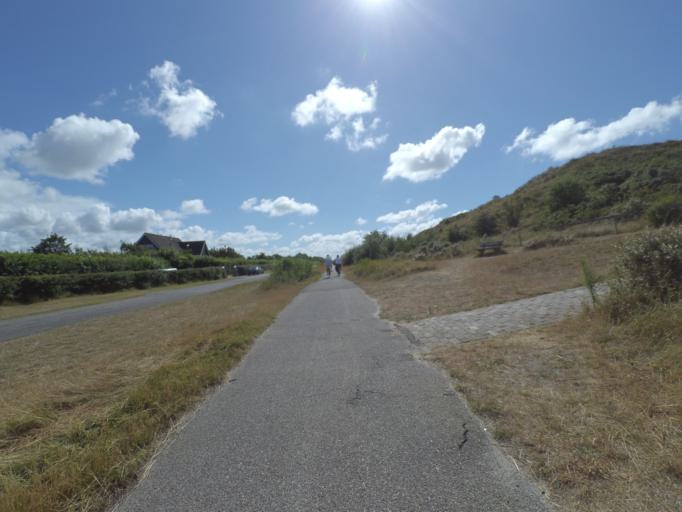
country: NL
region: North Holland
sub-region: Gemeente Texel
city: Den Burg
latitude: 53.1283
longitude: 4.8136
